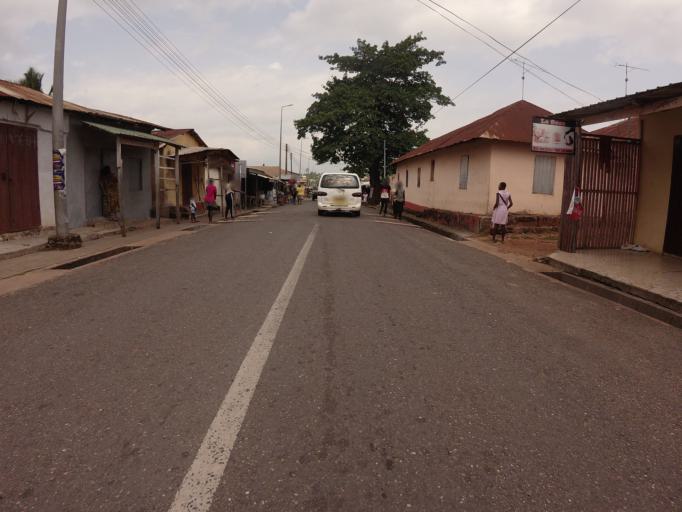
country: GH
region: Volta
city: Ho
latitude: 6.6166
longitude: 0.4693
